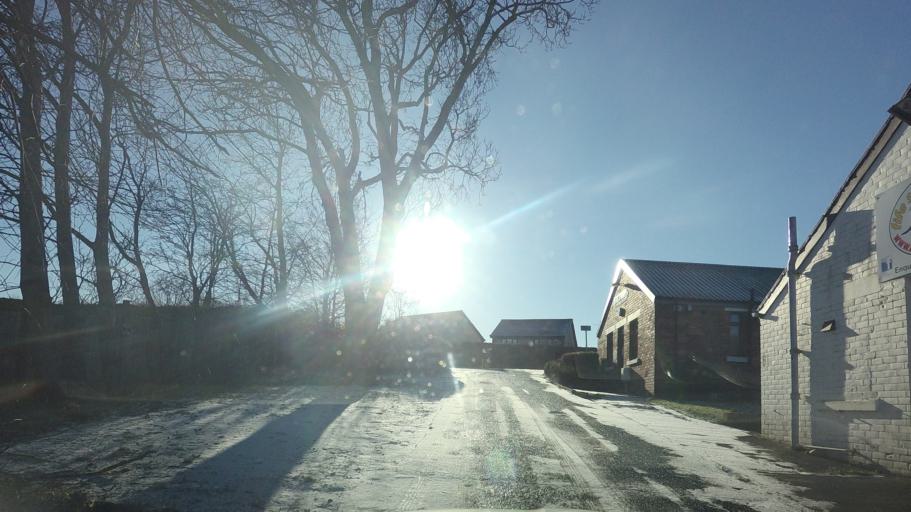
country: GB
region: Scotland
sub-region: Fife
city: Aberdour
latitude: 56.0449
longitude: -3.3434
